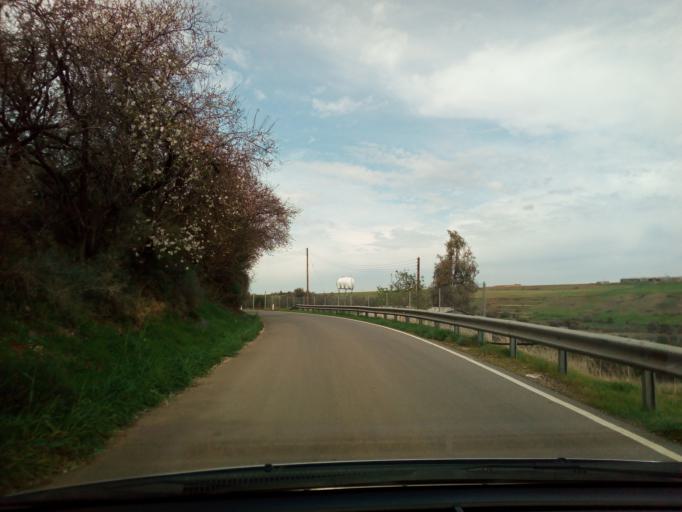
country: CY
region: Lefkosia
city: Astromeritis
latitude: 35.0972
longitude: 32.9855
